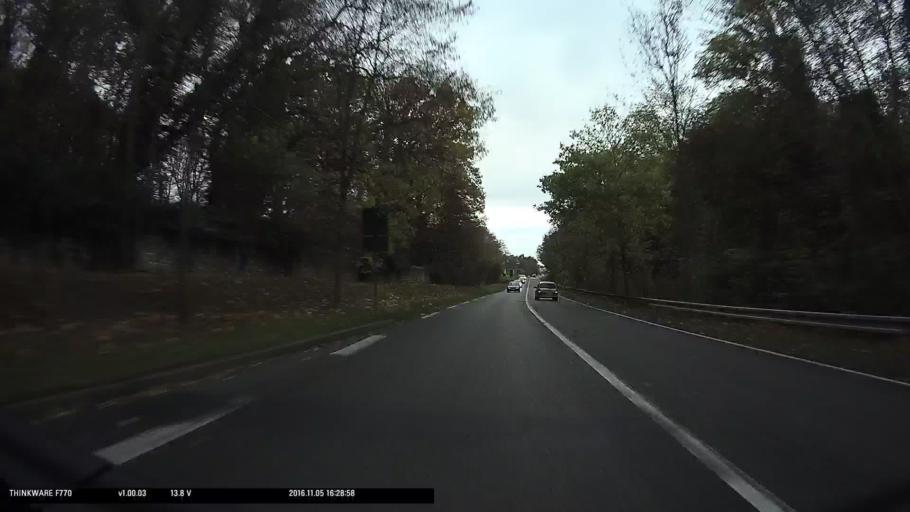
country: FR
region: Ile-de-France
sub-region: Departement du Val-d'Oise
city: Sagy
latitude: 49.0337
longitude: 1.9383
